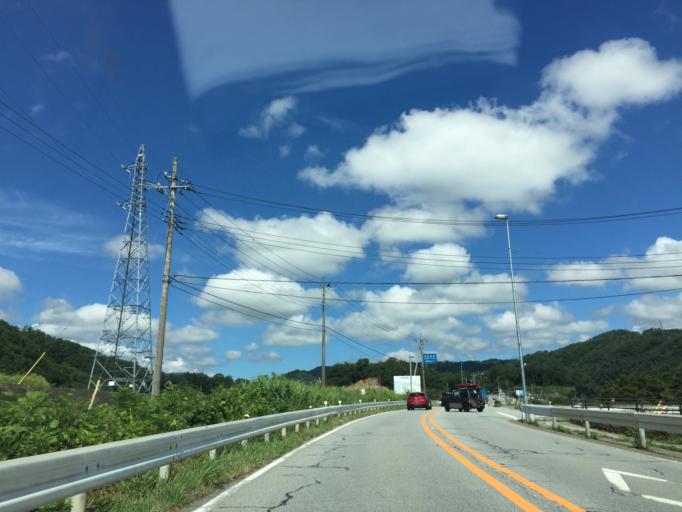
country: JP
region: Yamanashi
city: Nirasaki
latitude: 35.7991
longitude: 138.3572
